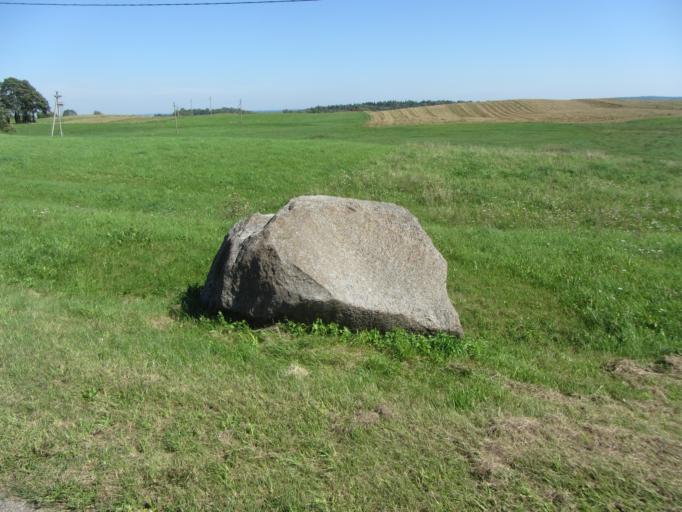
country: LT
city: Lazdijai
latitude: 54.2614
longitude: 23.6319
